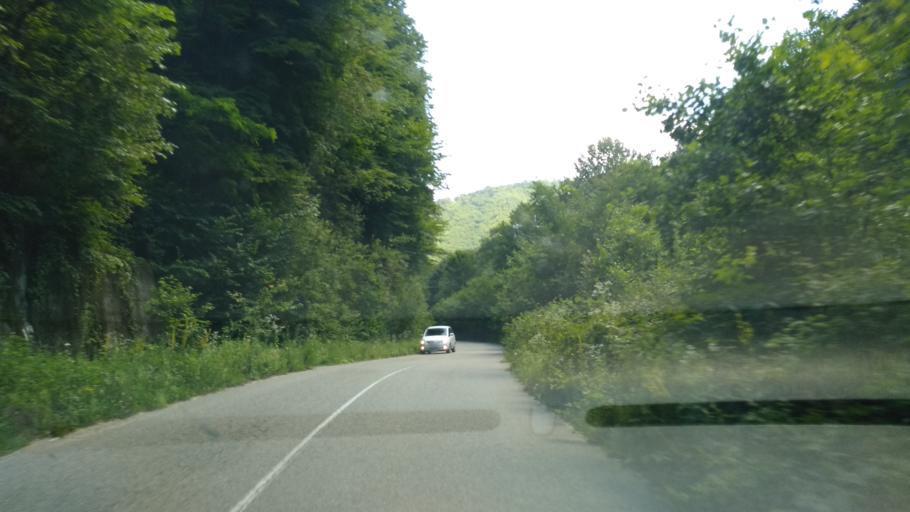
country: RO
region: Hunedoara
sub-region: Comuna Orastioara de Sus
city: Orastioara de Sus
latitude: 45.6664
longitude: 23.1710
